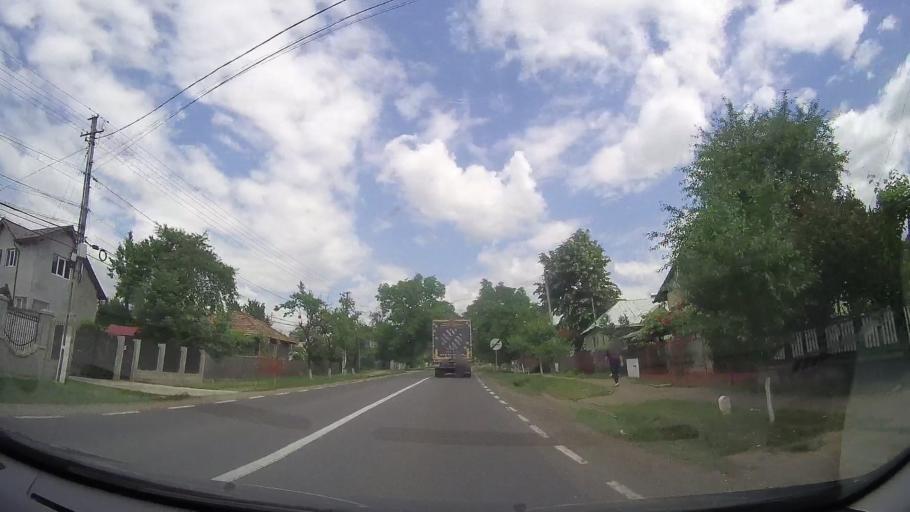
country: RO
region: Prahova
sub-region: Comuna Izvoarele
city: Homoraciu
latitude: 45.2630
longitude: 26.0149
